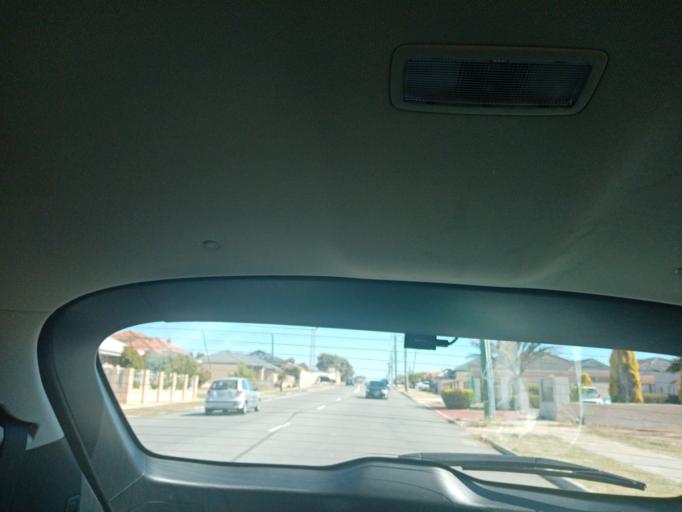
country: AU
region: Western Australia
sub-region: City of Cockburn
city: Spearwood
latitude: -32.1097
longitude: 115.7827
